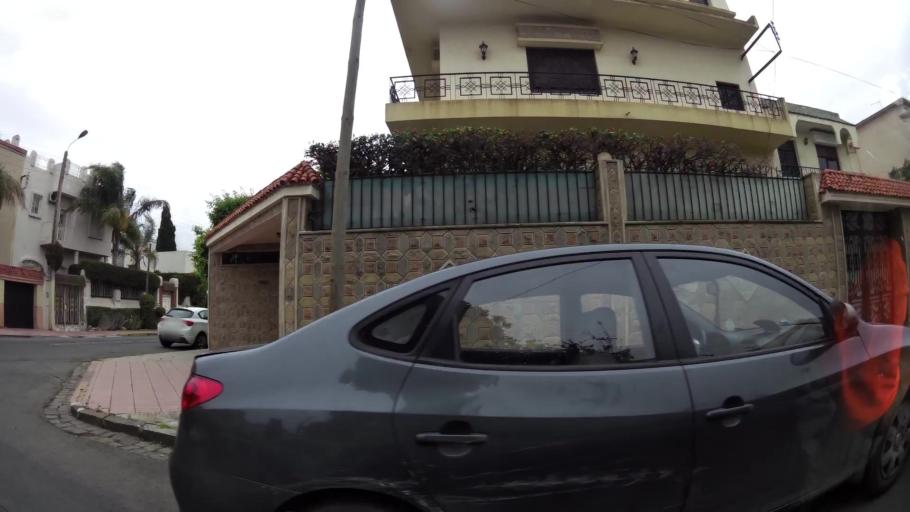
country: MA
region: Grand Casablanca
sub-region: Casablanca
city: Casablanca
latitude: 33.5648
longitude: -7.6168
